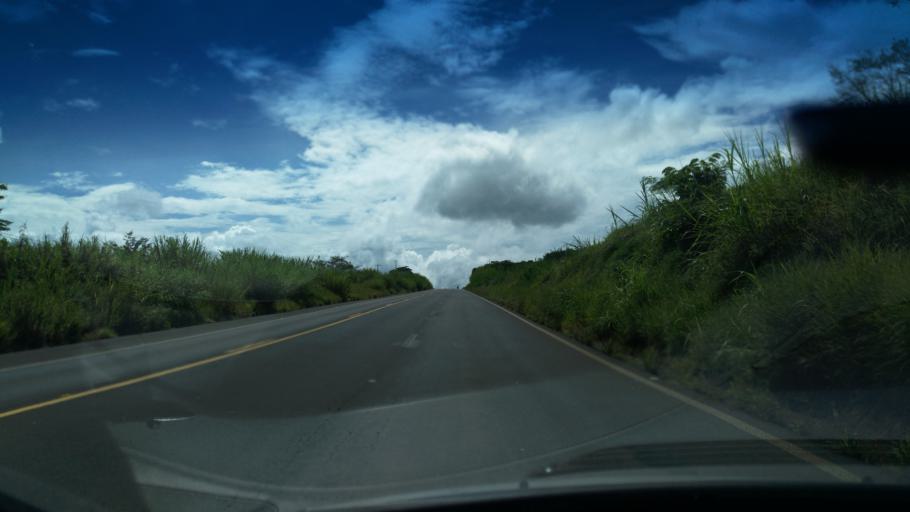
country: BR
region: Sao Paulo
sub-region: Santo Antonio Do Jardim
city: Espirito Santo do Pinhal
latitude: -22.1565
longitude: -46.7260
